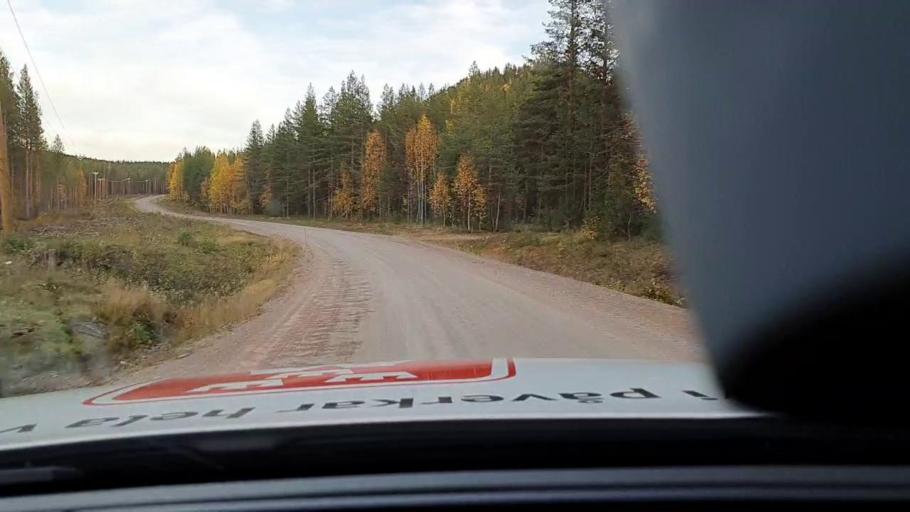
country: SE
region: Norrbotten
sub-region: Overkalix Kommun
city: OEverkalix
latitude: 66.3255
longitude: 22.6121
